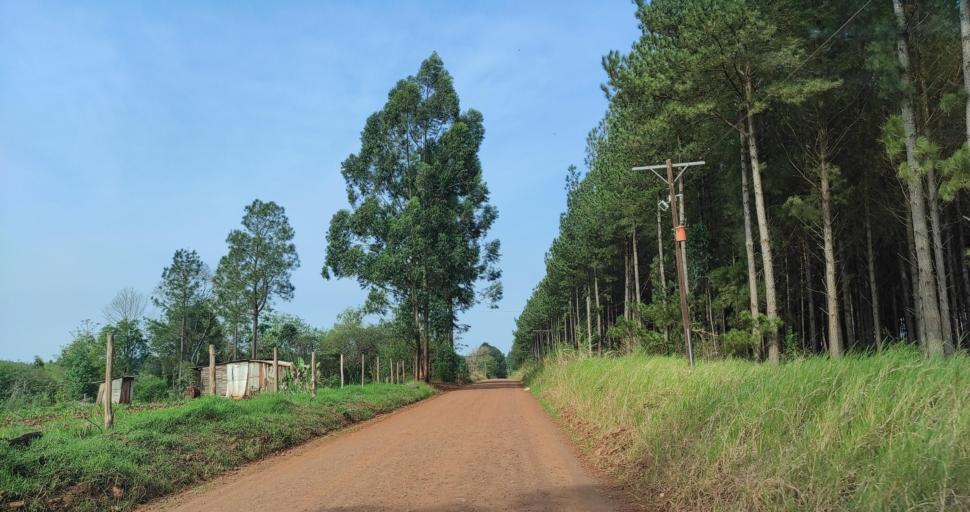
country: AR
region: Misiones
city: Capiovi
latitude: -26.8801
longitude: -55.0103
